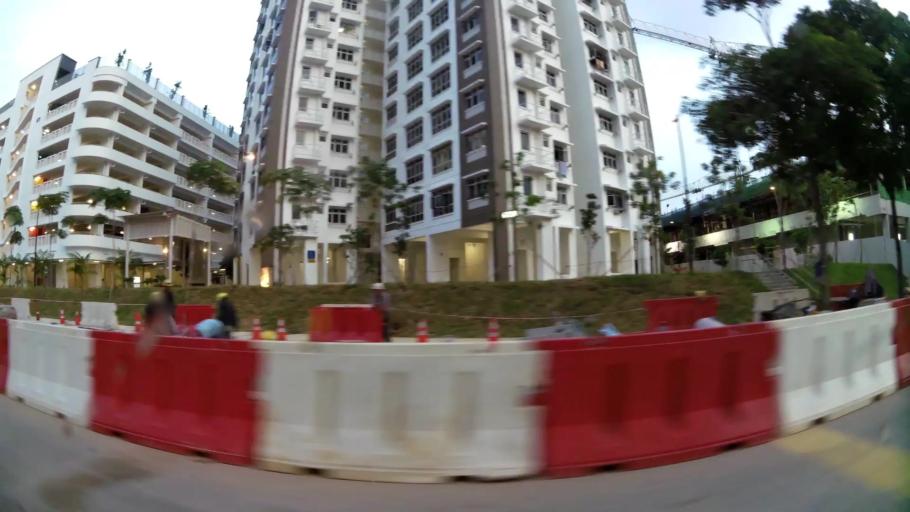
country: MY
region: Johor
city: Kampung Pasir Gudang Baru
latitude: 1.4189
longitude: 103.8409
